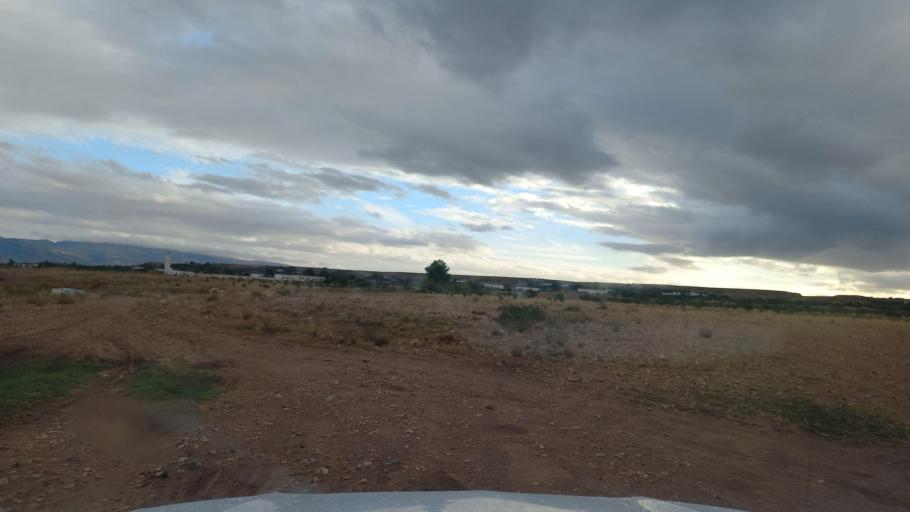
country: TN
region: Al Qasrayn
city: Kasserine
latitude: 35.2700
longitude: 8.9360
